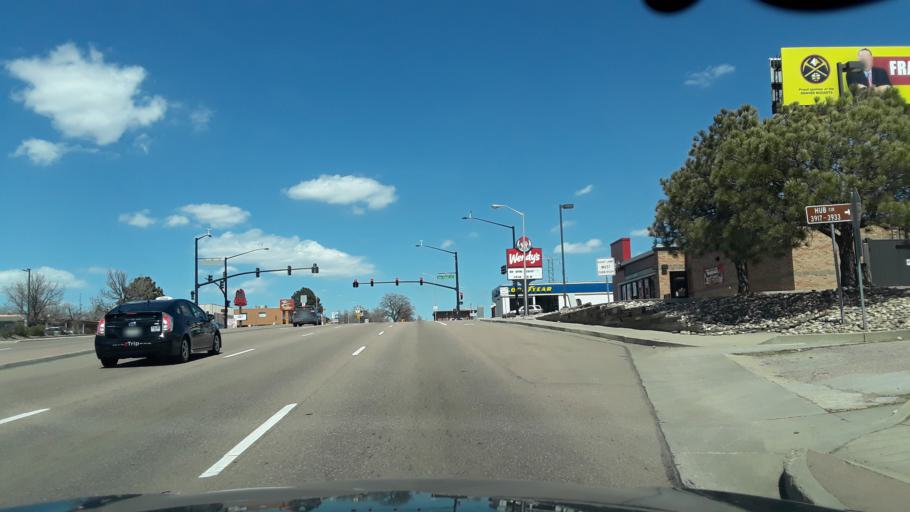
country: US
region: Colorado
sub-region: El Paso County
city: Cimarron Hills
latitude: 38.8503
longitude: -104.7572
